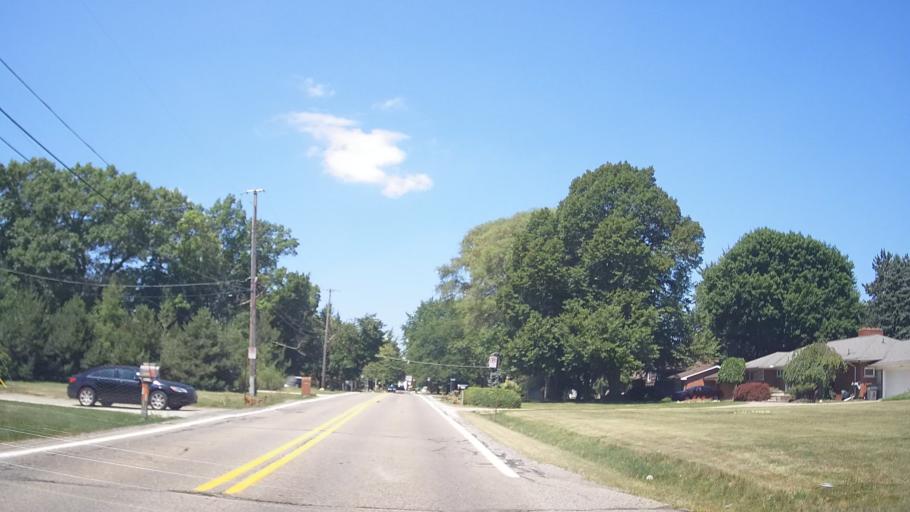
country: US
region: Michigan
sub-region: Macomb County
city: Clinton
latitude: 42.5884
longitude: -82.9091
